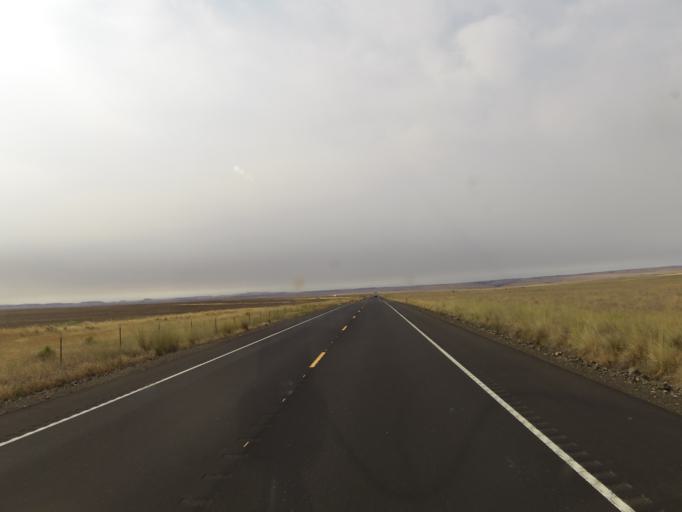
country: US
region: Oregon
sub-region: Sherman County
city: Moro
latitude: 45.1836
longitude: -120.6953
